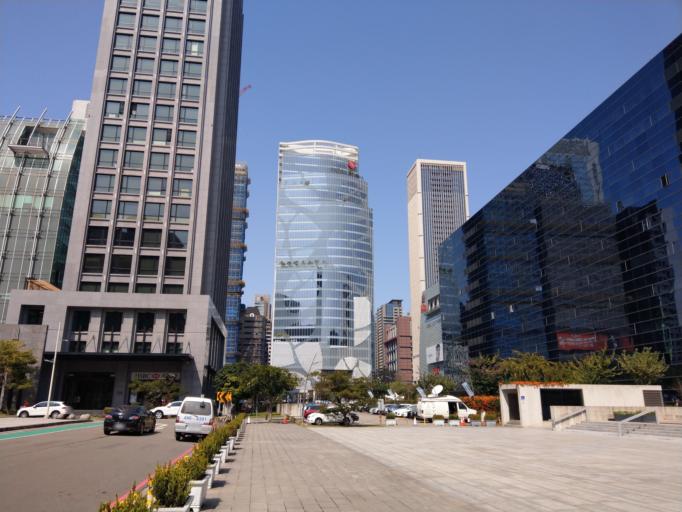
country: TW
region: Taiwan
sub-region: Taichung City
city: Taichung
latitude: 24.1612
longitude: 120.6465
